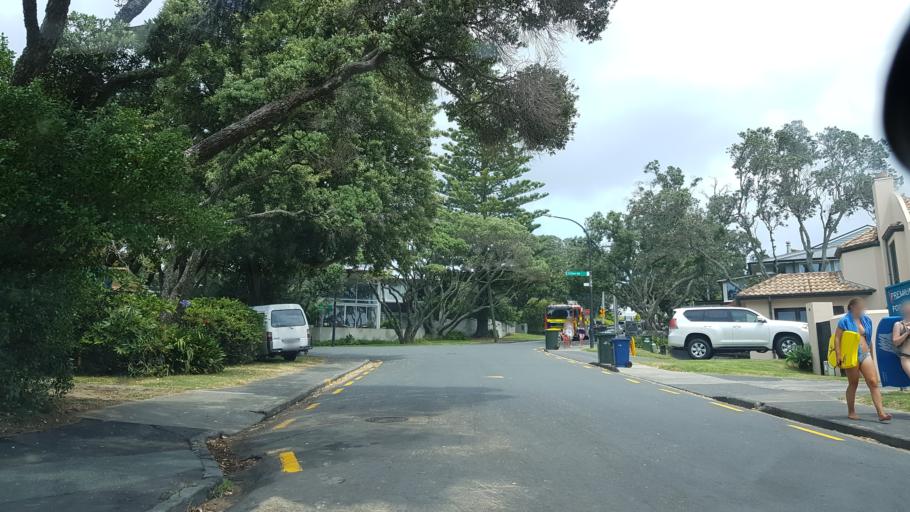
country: NZ
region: Auckland
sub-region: Auckland
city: North Shore
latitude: -36.7939
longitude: 174.7815
